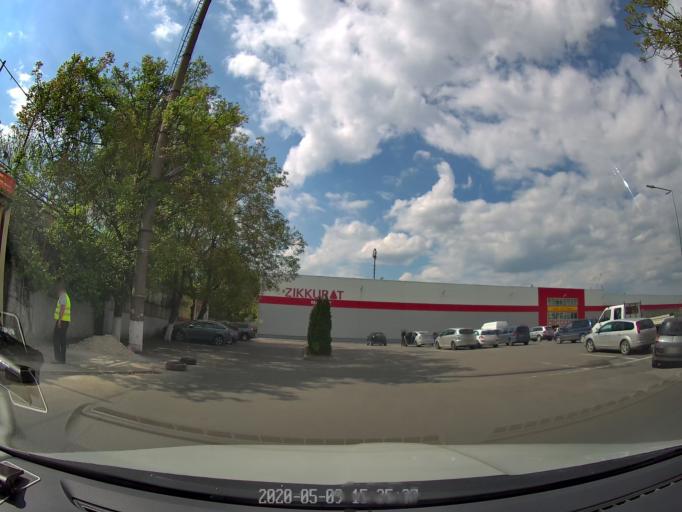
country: MD
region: Chisinau
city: Chisinau
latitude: 46.9786
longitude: 28.8794
